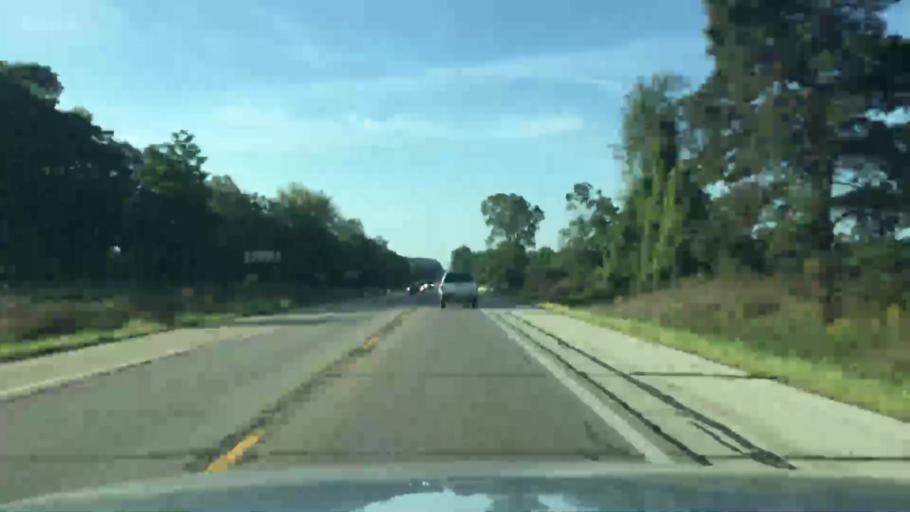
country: US
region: Michigan
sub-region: Jackson County
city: Vandercook Lake
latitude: 42.1019
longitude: -84.3639
